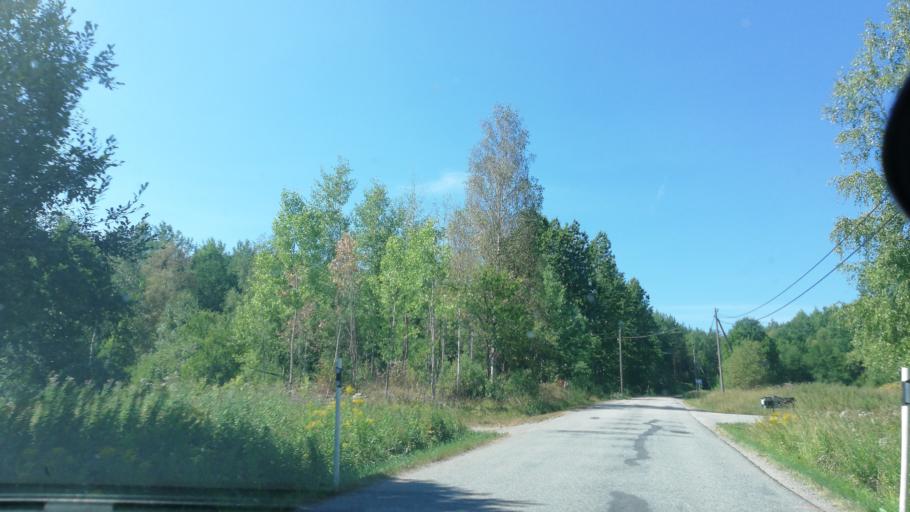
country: SE
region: OEstergoetland
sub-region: Finspangs Kommun
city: Finspang
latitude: 58.7289
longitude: 15.7475
